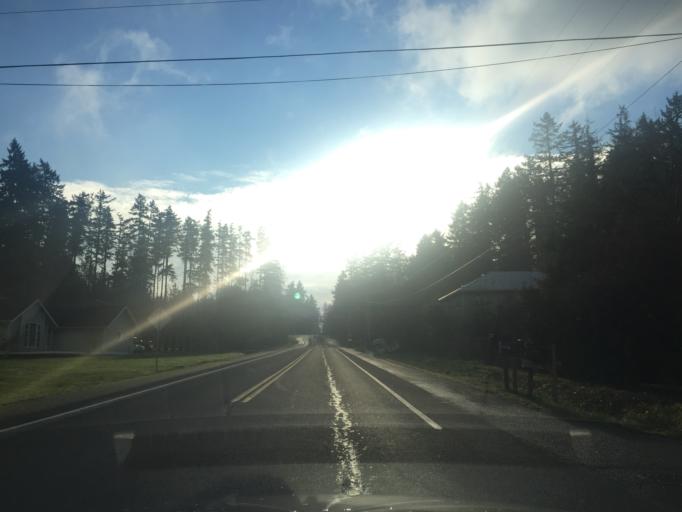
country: US
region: Washington
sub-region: Thurston County
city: Olympia
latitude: 47.1381
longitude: -122.9016
